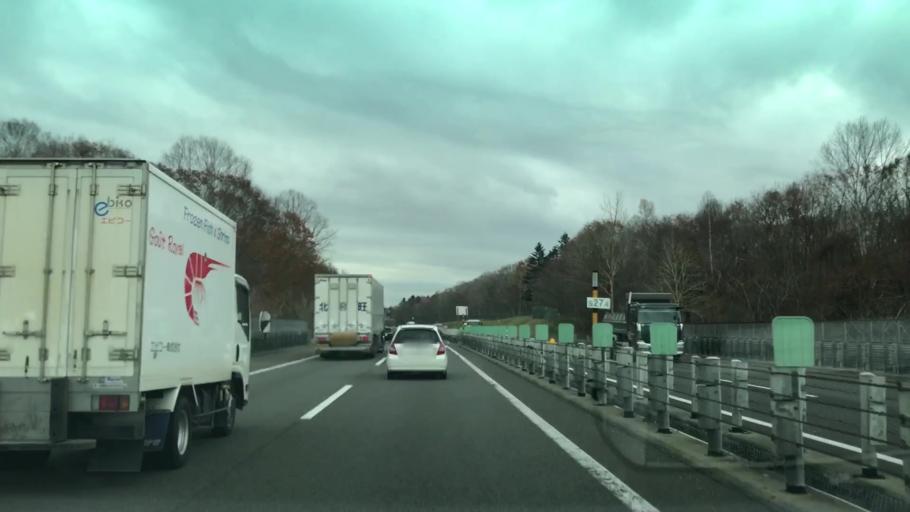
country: JP
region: Hokkaido
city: Chitose
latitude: 42.8619
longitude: 141.5588
